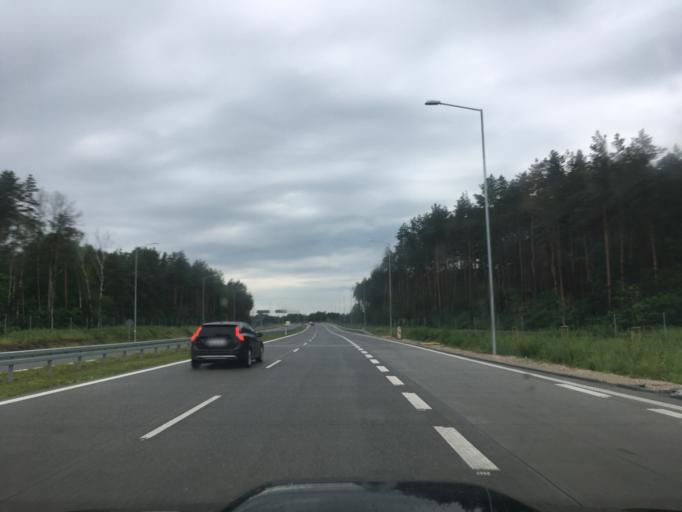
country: PL
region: Masovian Voivodeship
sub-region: Powiat piaseczynski
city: Gora Kalwaria
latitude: 51.9728
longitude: 21.1927
